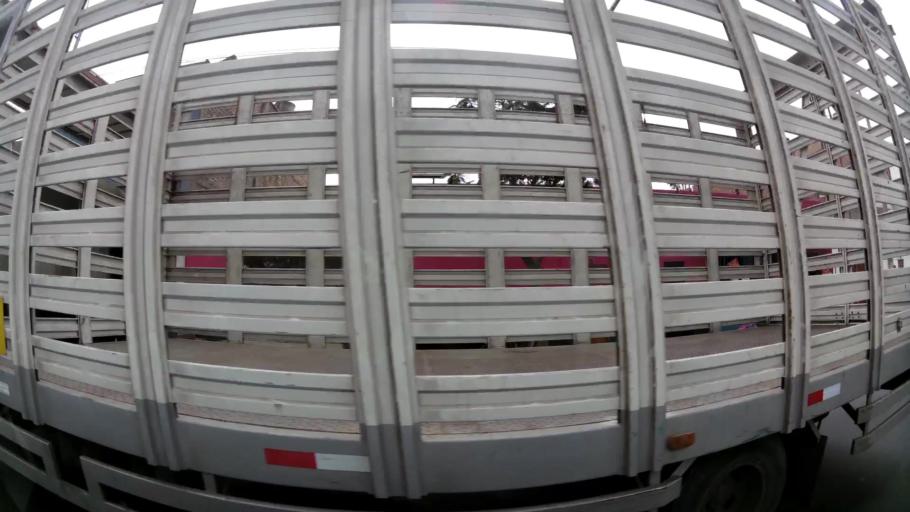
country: PE
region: Lima
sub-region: Lima
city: Independencia
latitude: -11.9711
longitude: -76.9955
